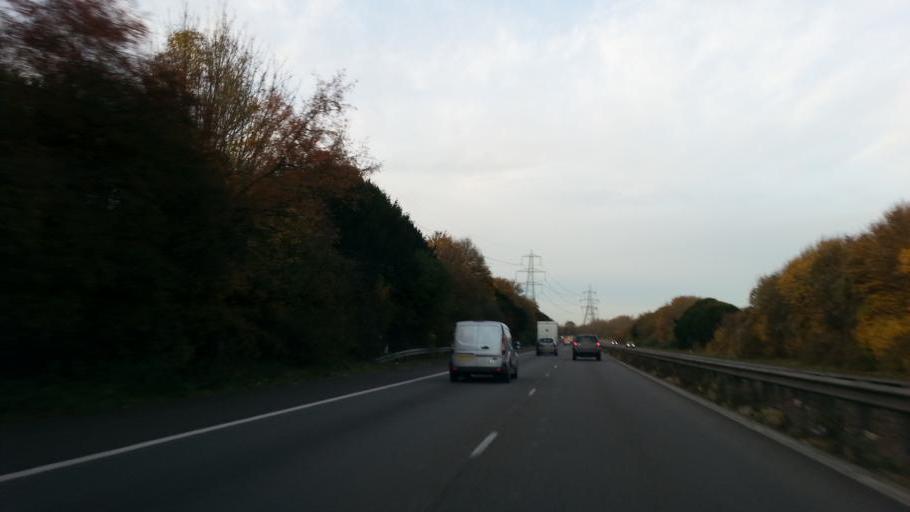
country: GB
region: England
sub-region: Hertfordshire
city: Baldock
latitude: 51.9938
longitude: -0.1978
